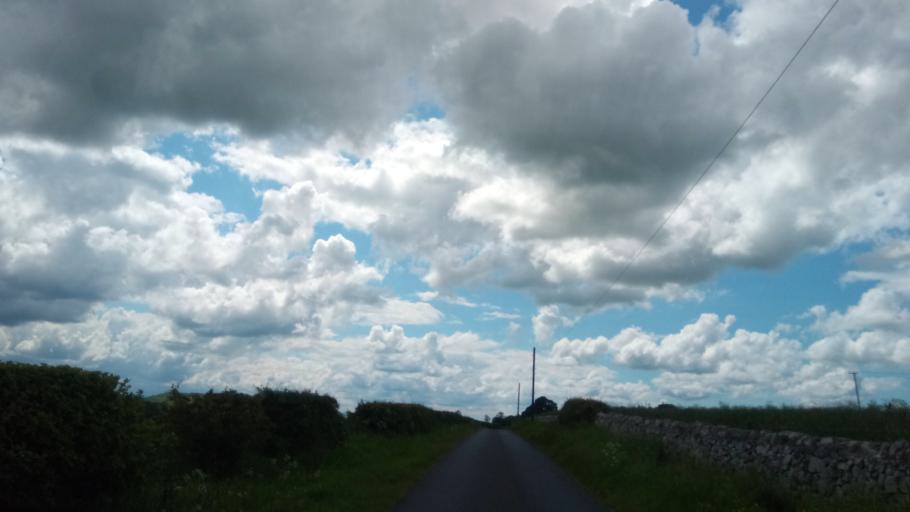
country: GB
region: Scotland
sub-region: The Scottish Borders
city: Coldstream
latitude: 55.5804
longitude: -2.3124
